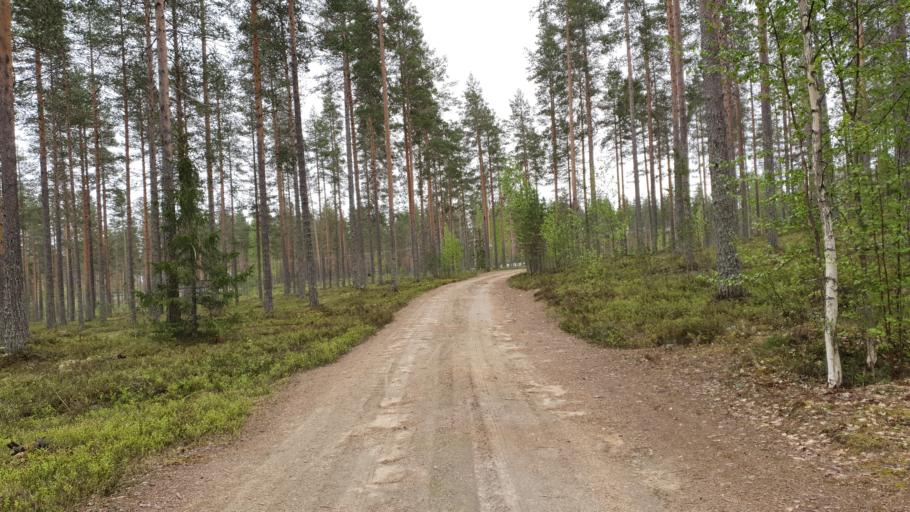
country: FI
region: Kainuu
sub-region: Kehys-Kainuu
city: Kuhmo
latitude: 64.0982
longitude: 29.4654
